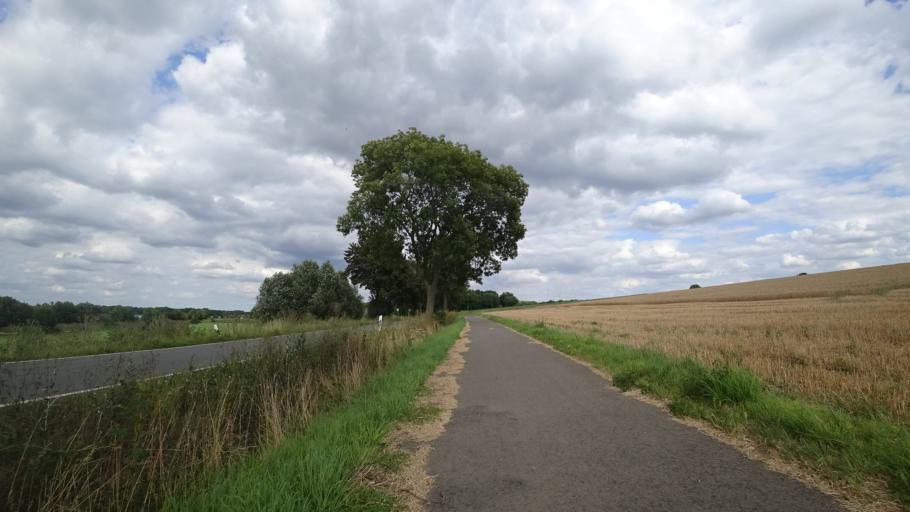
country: DE
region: Lower Saxony
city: Stolzenau
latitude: 52.4677
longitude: 9.0739
